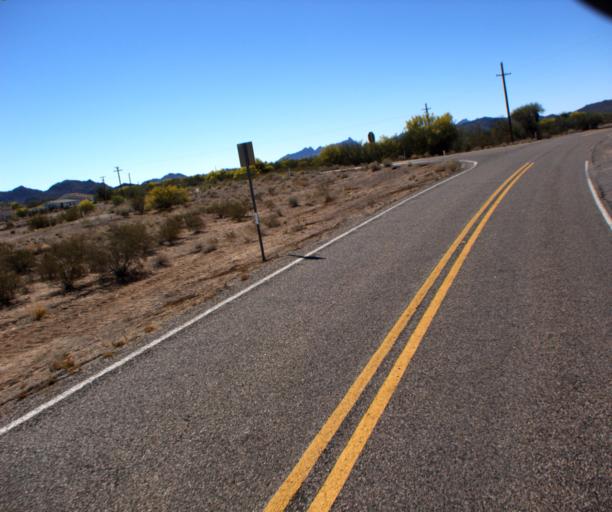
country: US
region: Arizona
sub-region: Pima County
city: Ajo
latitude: 32.2682
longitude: -112.7390
